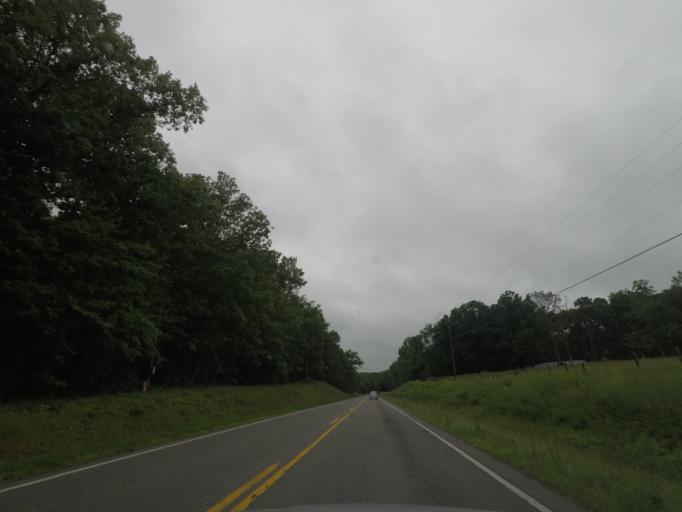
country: US
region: Virginia
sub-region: Fluvanna County
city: Palmyra
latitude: 37.8184
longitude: -78.2627
